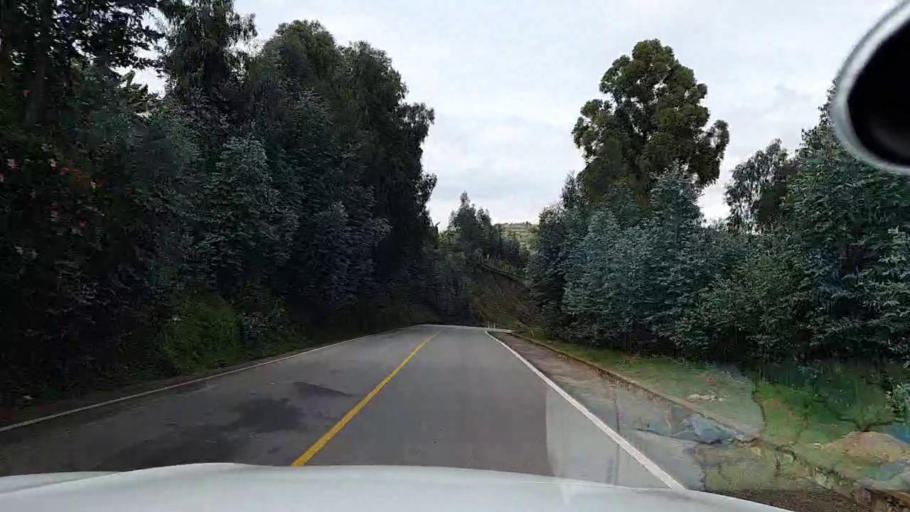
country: RW
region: Southern Province
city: Nzega
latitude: -2.5047
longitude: 29.5075
